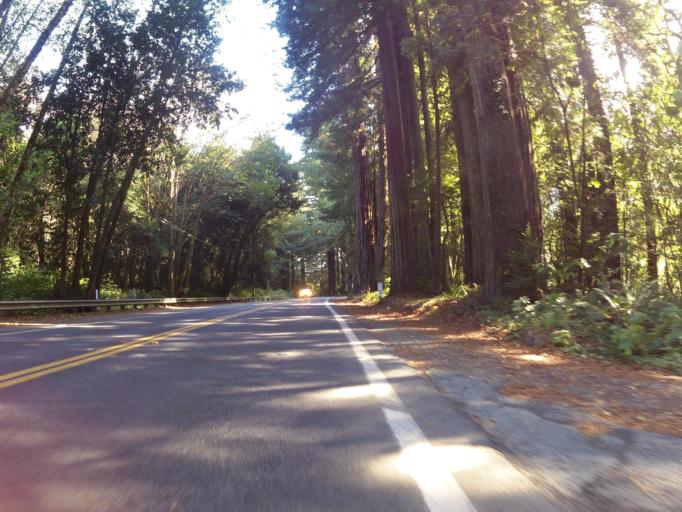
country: US
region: California
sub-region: Del Norte County
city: Bertsch-Oceanview
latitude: 41.8460
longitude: -124.1166
